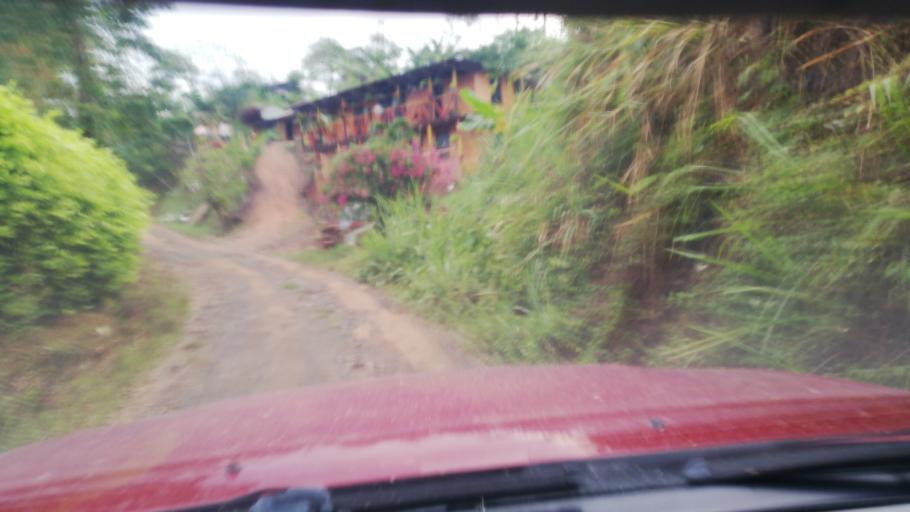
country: CO
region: Risaralda
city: Balboa
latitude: 4.8883
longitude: -75.9588
